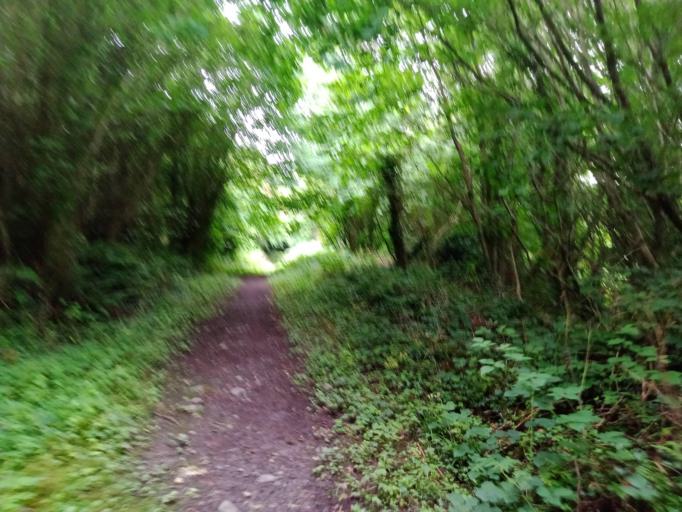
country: IE
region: Leinster
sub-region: Kilkenny
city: Ballyragget
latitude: 52.8259
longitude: -7.4015
